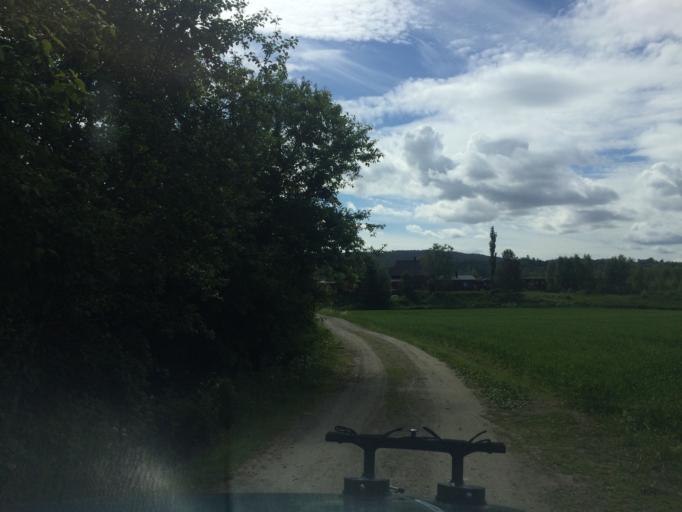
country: NO
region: Nord-Trondelag
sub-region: Overhalla
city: Ranemsletta
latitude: 64.4665
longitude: 12.0607
